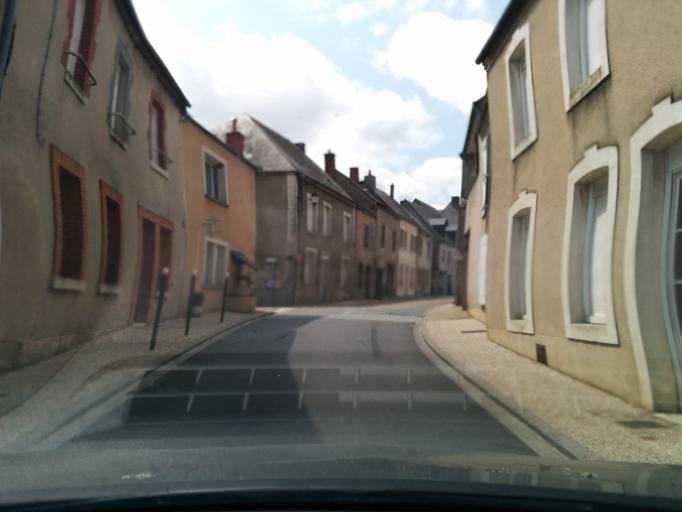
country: FR
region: Centre
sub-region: Departement du Cher
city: Henrichemont
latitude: 47.3447
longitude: 2.4862
